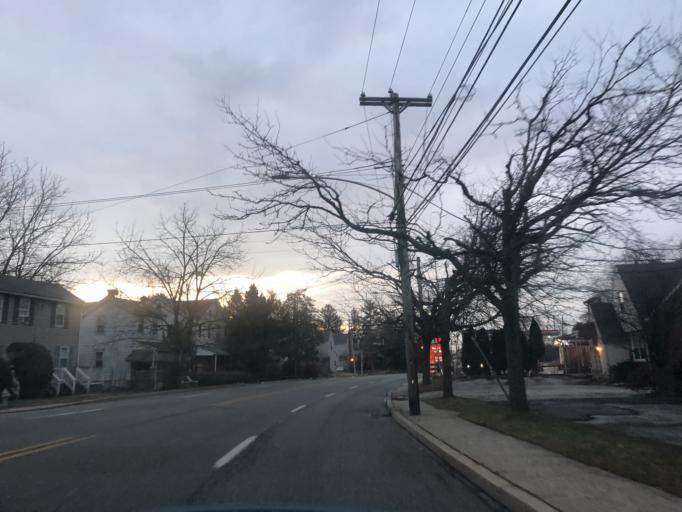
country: US
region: Pennsylvania
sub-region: Montgomery County
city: Bryn Mawr
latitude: 40.0124
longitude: -75.3161
